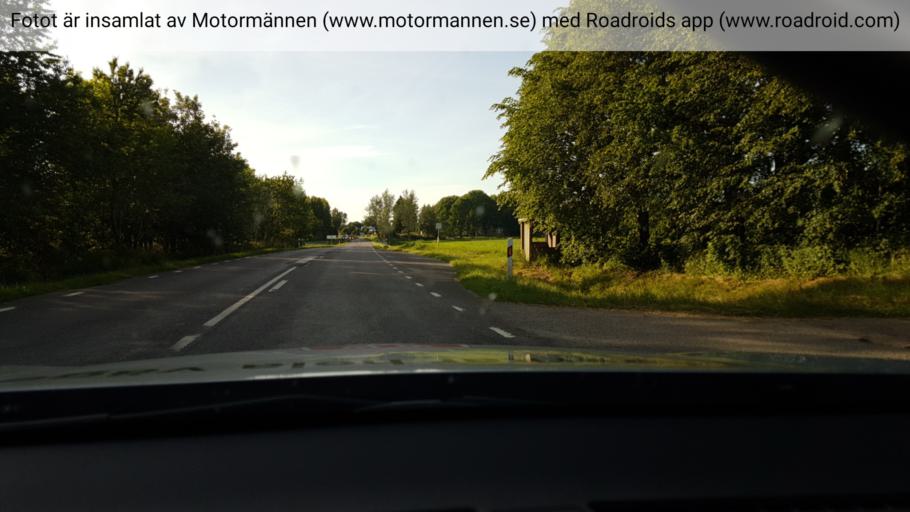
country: SE
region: Vaestra Goetaland
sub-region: Falkopings Kommun
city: Falkoeping
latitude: 58.0663
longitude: 13.5286
